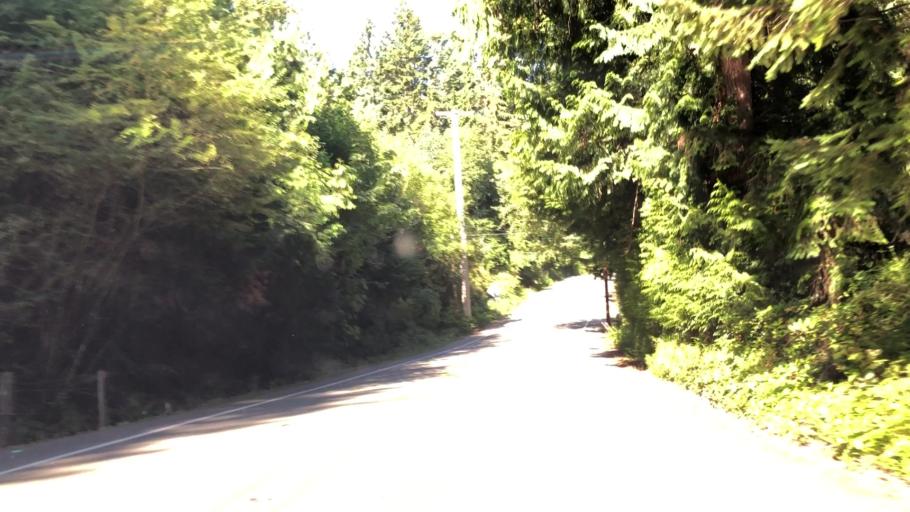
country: US
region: Washington
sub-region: Kitsap County
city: Kingston
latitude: 47.7730
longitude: -122.5037
